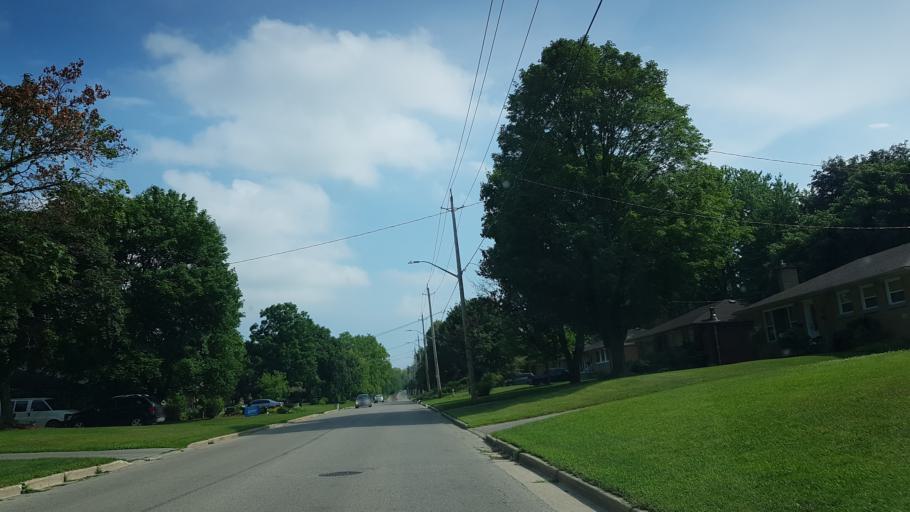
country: CA
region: Ontario
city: Delaware
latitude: 42.9585
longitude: -81.3417
